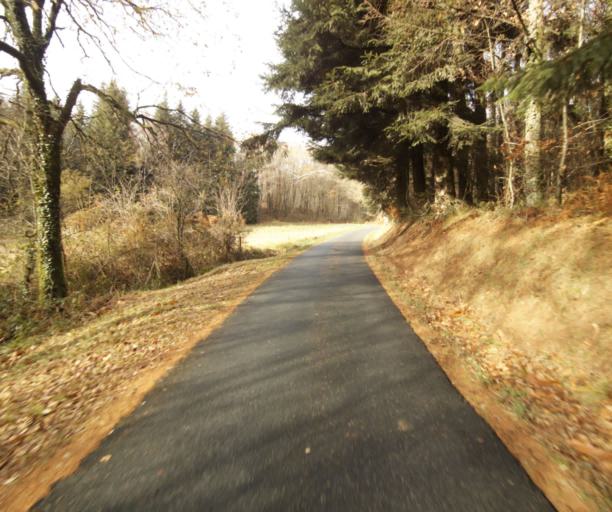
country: FR
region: Limousin
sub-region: Departement de la Correze
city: Sainte-Fortunade
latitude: 45.1798
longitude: 1.7472
